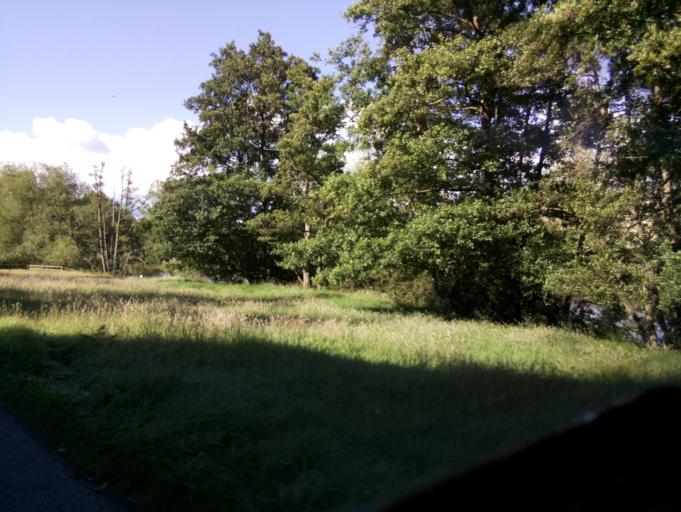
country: GB
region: England
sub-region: Herefordshire
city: Yatton
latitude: 51.9644
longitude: -2.5593
